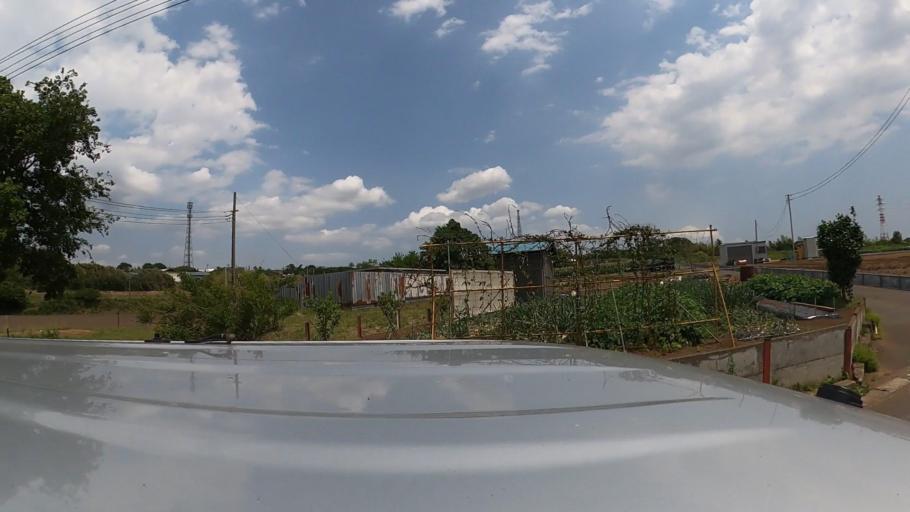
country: JP
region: Kanagawa
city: Chigasaki
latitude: 35.3872
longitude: 139.4188
